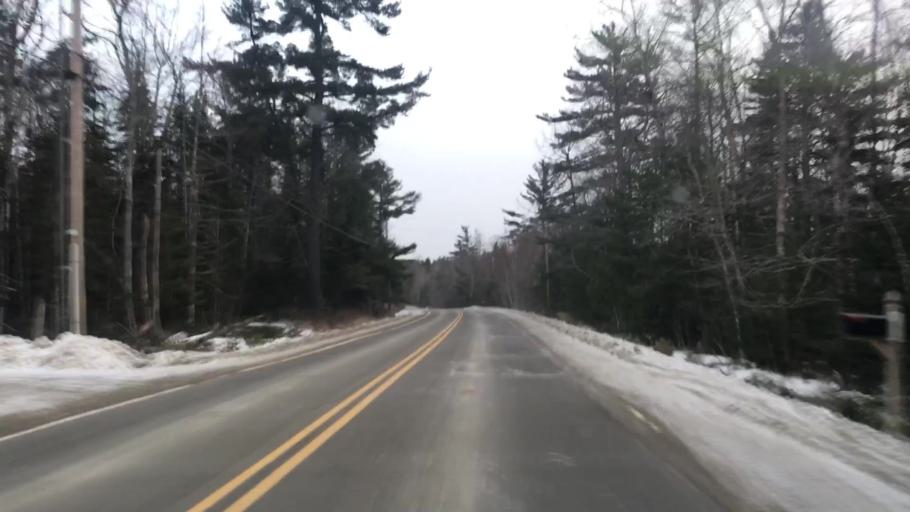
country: US
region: Maine
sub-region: Hancock County
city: Ellsworth
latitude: 44.6180
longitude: -68.3843
